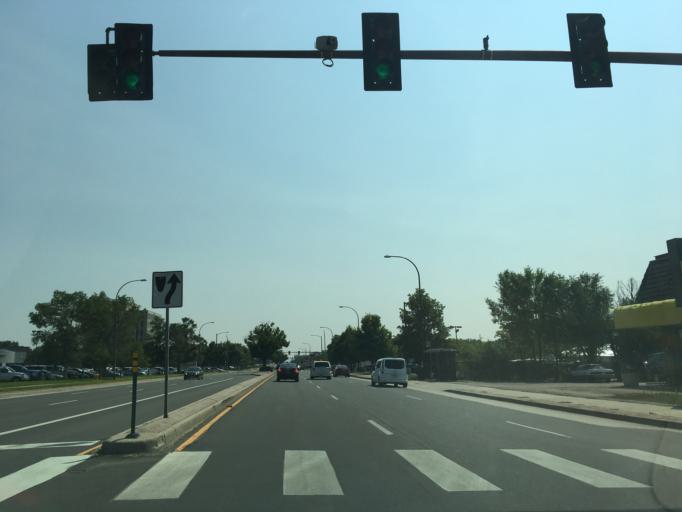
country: US
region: Colorado
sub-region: Jefferson County
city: Applewood
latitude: 39.7402
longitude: -105.1194
